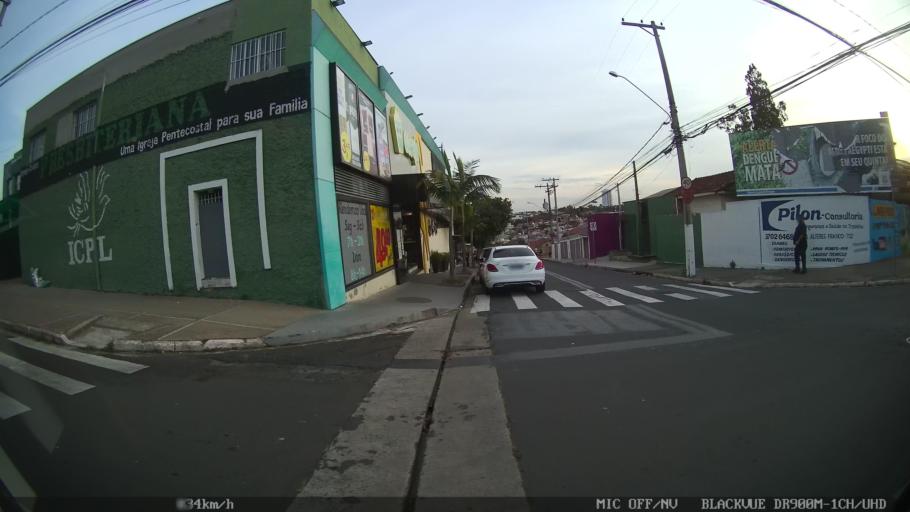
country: BR
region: Sao Paulo
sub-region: Limeira
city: Limeira
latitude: -22.5761
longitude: -47.4106
